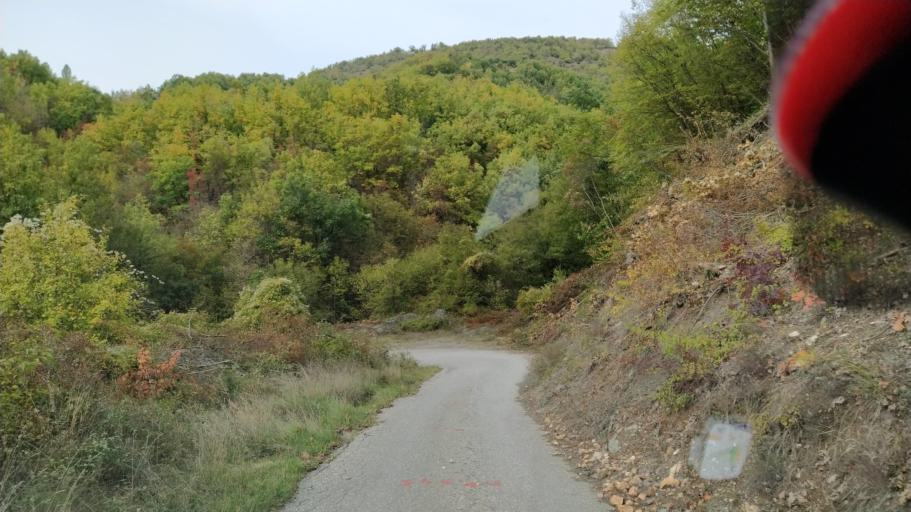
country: MK
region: Strumica
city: Veljusa
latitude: 41.5119
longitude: 22.4856
